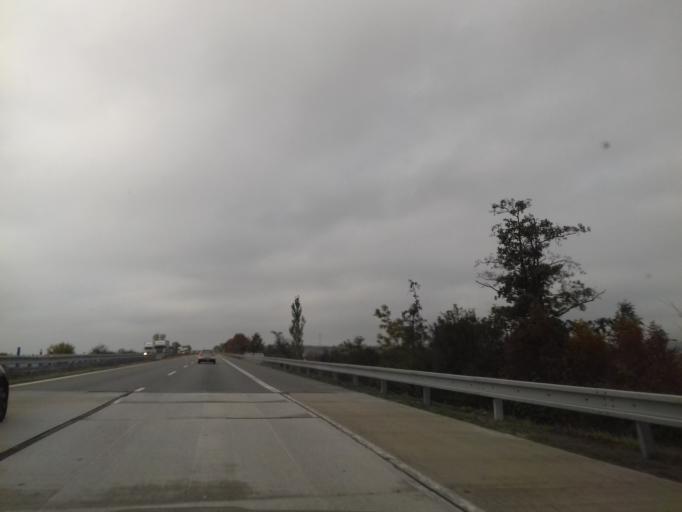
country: CZ
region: South Moravian
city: Rakvice
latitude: 48.8810
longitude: 16.8144
